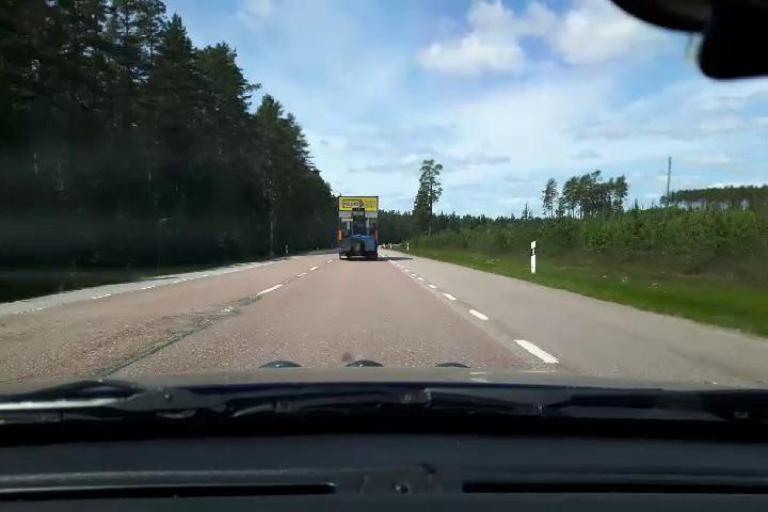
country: SE
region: Uppsala
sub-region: Osthammars Kommun
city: Bjorklinge
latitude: 60.1181
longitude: 17.5153
